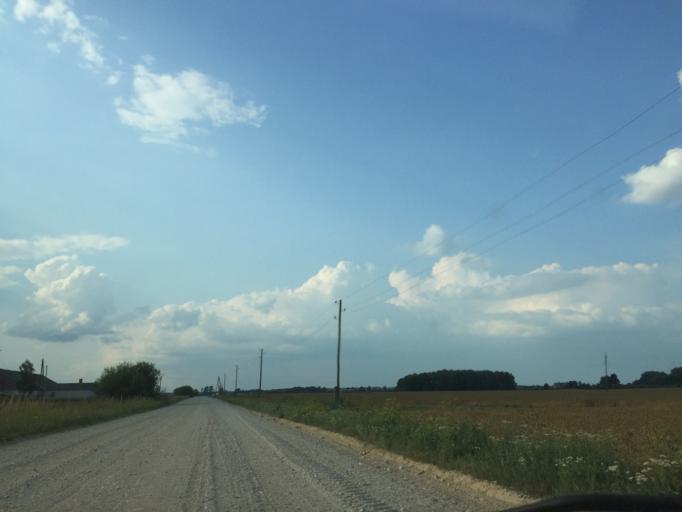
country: LT
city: Zagare
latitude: 56.4570
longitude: 23.1619
